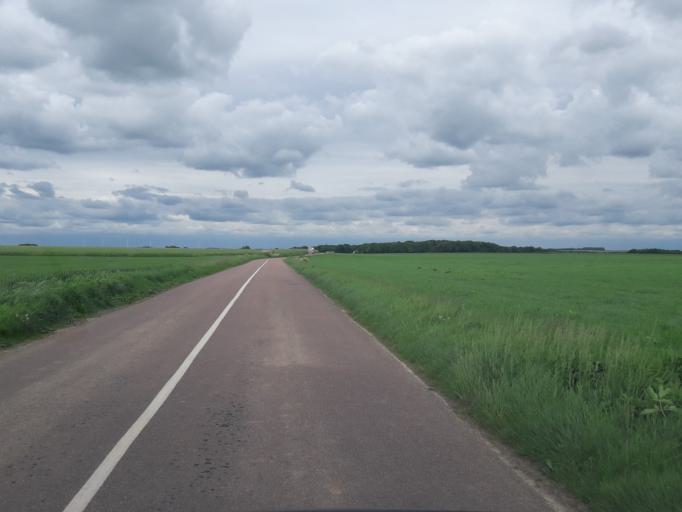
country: FR
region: Ile-de-France
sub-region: Departement de l'Essonne
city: Saclas
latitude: 48.3429
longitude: 2.1312
